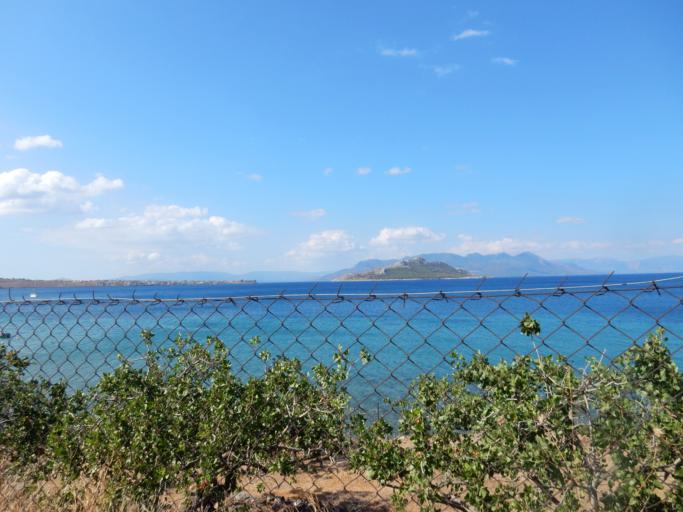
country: GR
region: Attica
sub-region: Nomos Piraios
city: Aegina
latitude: 37.7216
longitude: 23.4563
